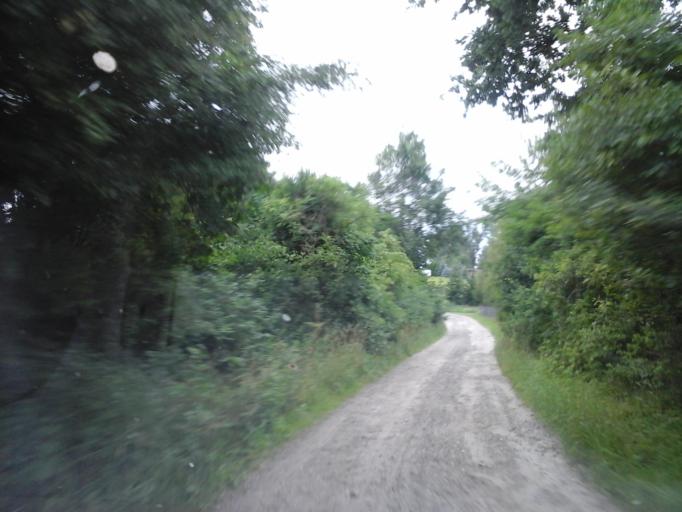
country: PL
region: West Pomeranian Voivodeship
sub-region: Powiat choszczenski
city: Krzecin
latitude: 53.0761
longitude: 15.5631
